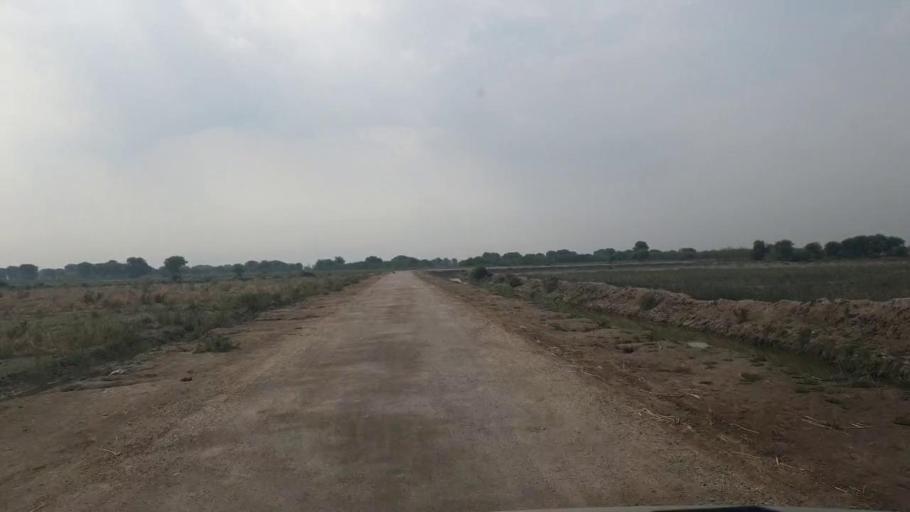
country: PK
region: Sindh
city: Talhar
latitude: 24.8641
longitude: 68.8347
